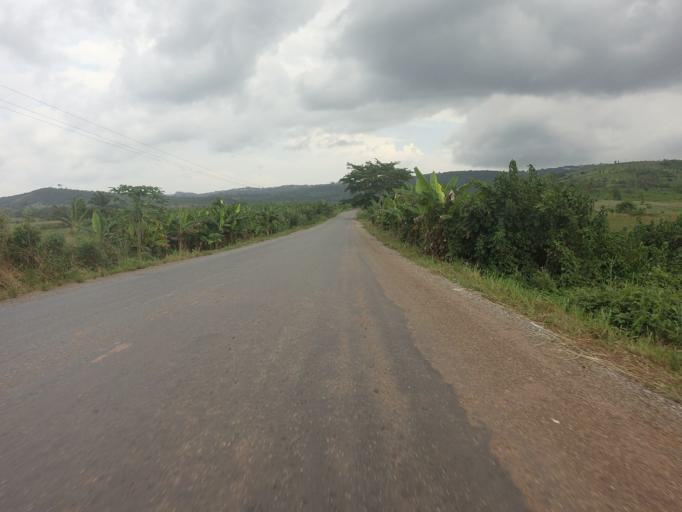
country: GH
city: Akropong
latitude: 5.9611
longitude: -0.1386
